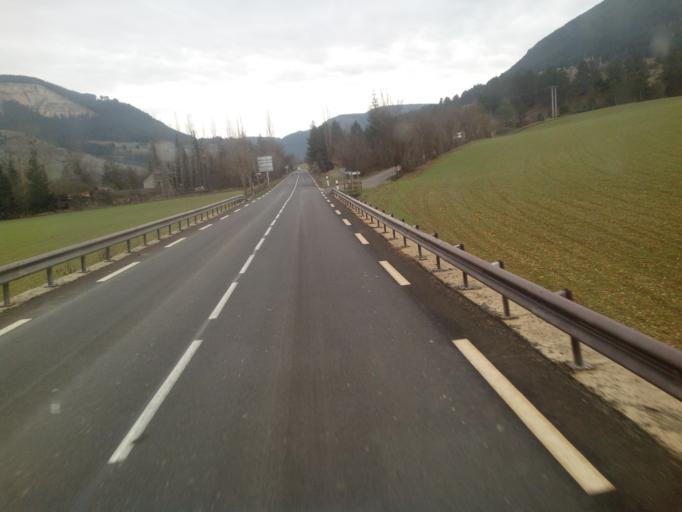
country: FR
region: Languedoc-Roussillon
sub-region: Departement de la Lozere
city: Mende
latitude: 44.4763
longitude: 3.4985
